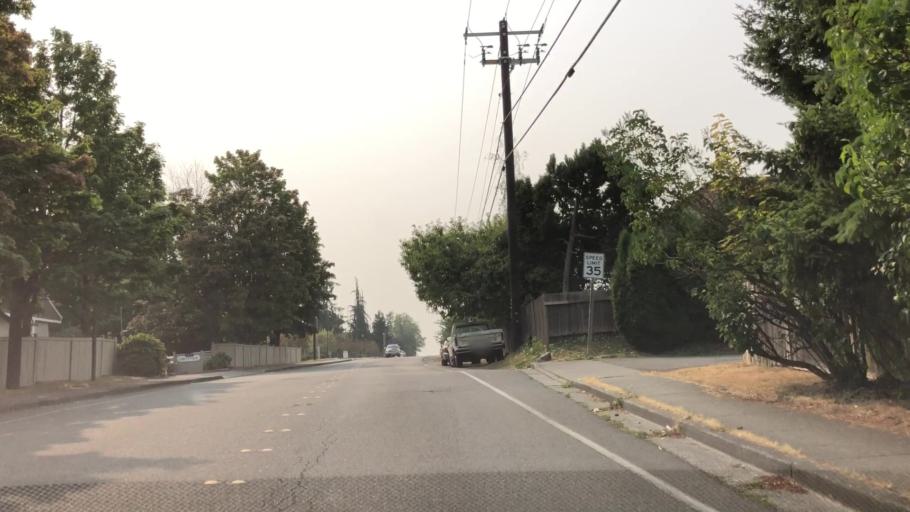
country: US
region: Washington
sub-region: Snohomish County
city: Alderwood Manor
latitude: 47.8573
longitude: -122.2811
